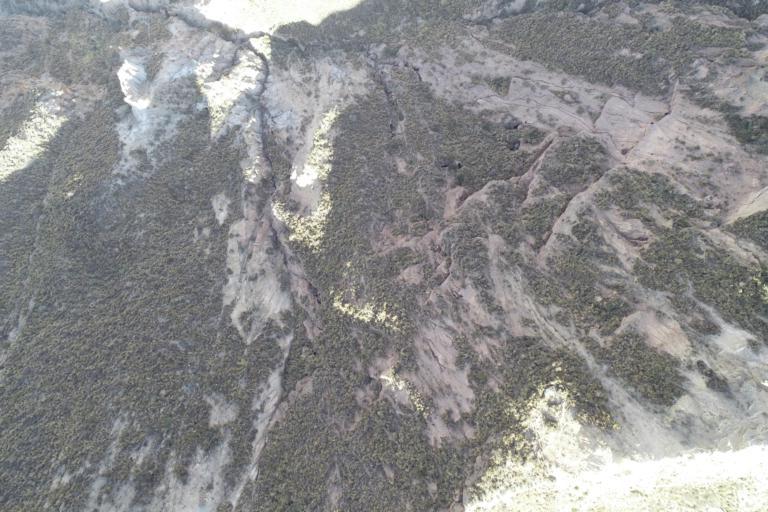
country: BO
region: La Paz
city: La Paz
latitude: -16.5513
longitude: -68.1046
